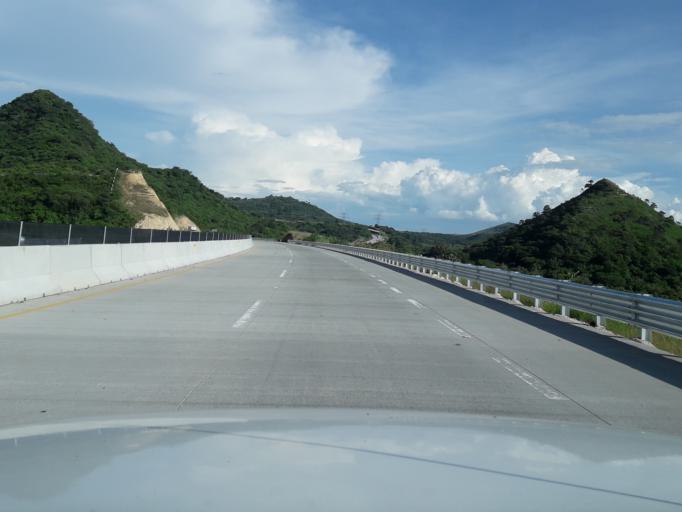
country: MX
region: Jalisco
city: Tala
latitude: 20.5999
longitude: -103.6761
